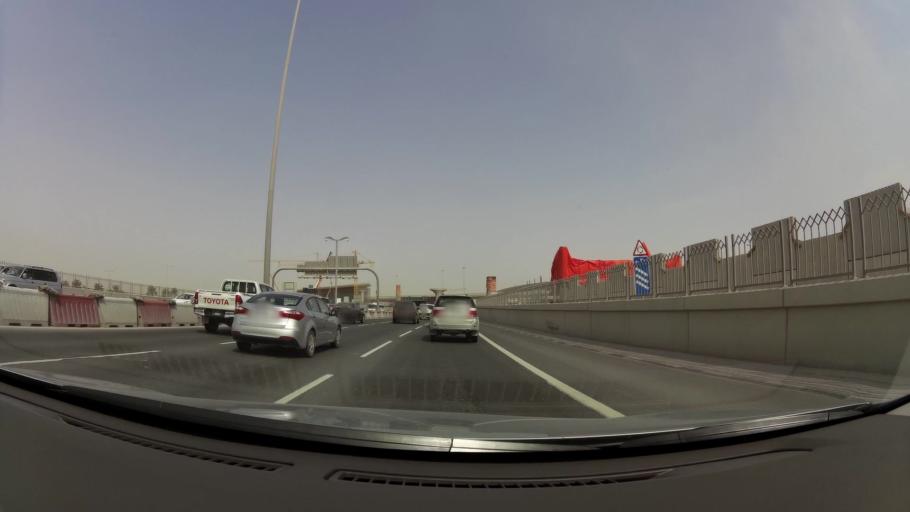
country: QA
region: Baladiyat ad Dawhah
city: Doha
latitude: 25.2921
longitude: 51.4764
